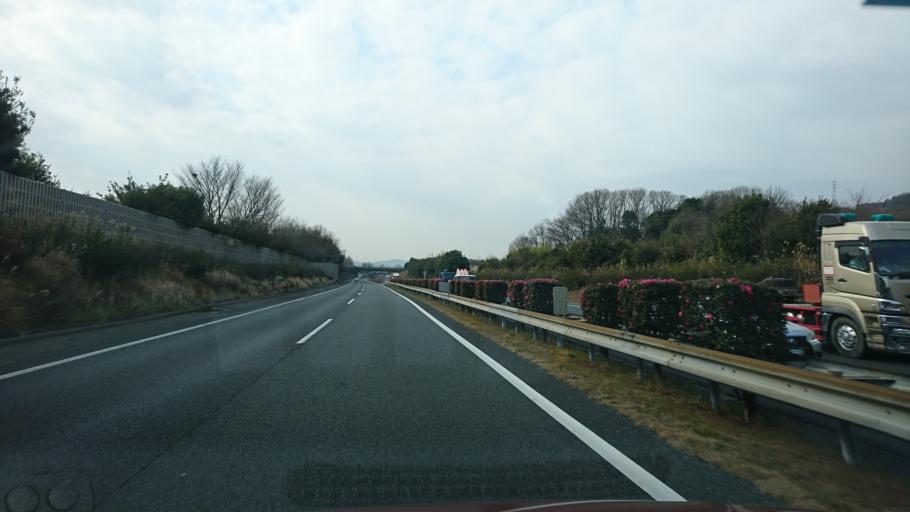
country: JP
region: Hiroshima
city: Kannabecho-yahiro
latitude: 34.5202
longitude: 133.4243
